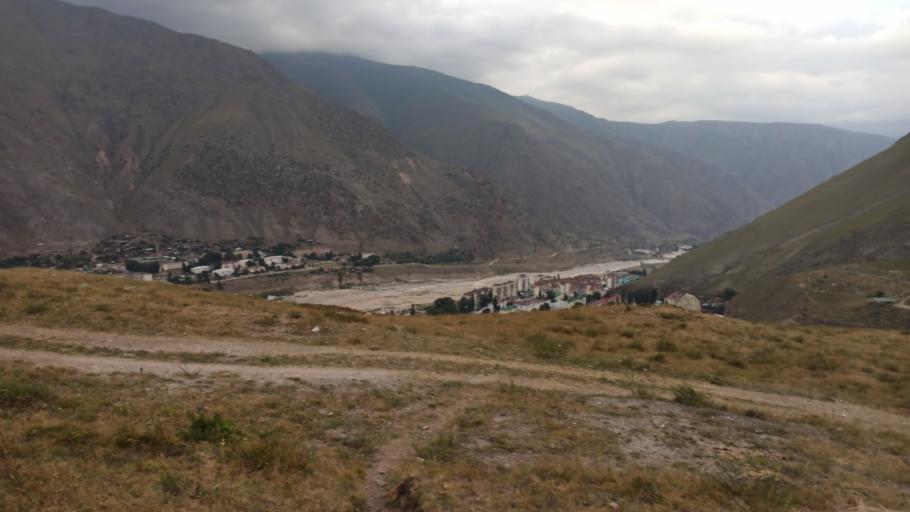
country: RU
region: Kabardino-Balkariya
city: Tyrnyauz
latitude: 43.3916
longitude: 42.9267
